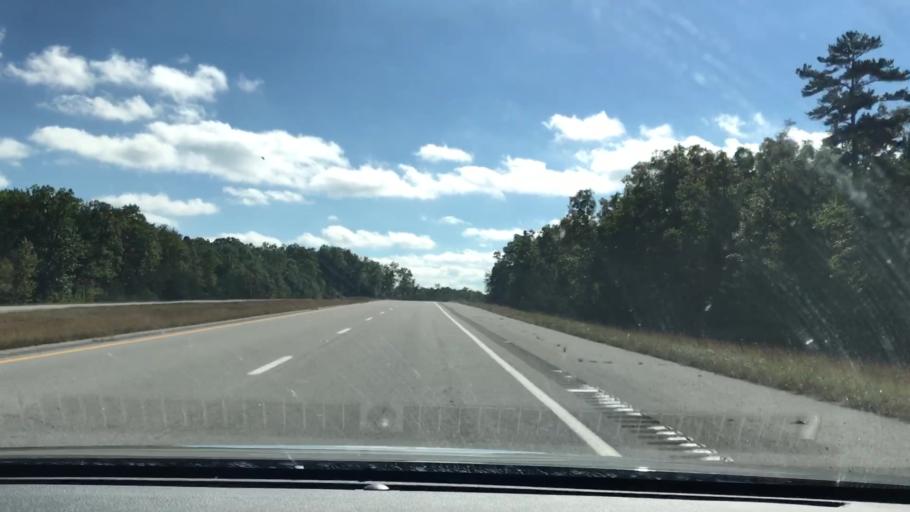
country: US
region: Tennessee
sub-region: Fentress County
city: Grimsley
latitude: 36.3352
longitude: -84.9562
